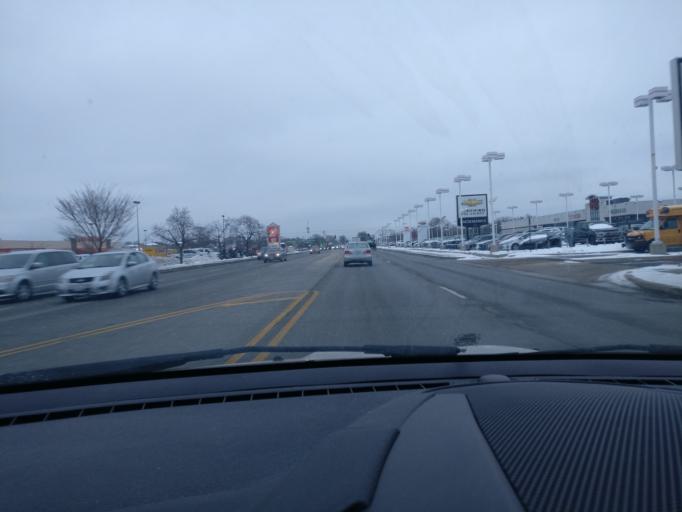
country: US
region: Illinois
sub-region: Cook County
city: Park Ridge
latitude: 42.0399
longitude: -87.8443
